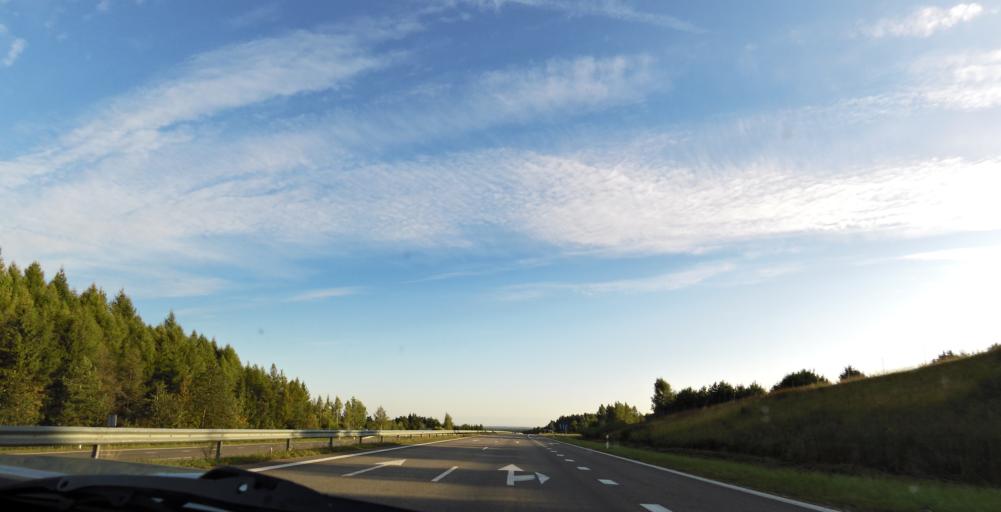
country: LT
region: Vilnius County
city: Ukmerge
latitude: 55.2257
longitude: 24.8178
